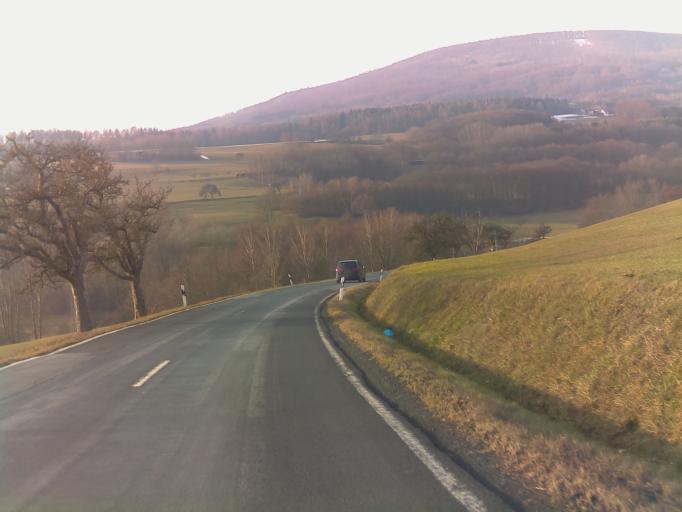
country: DE
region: Bavaria
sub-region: Regierungsbezirk Unterfranken
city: Sandberg
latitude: 50.3438
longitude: 10.0055
